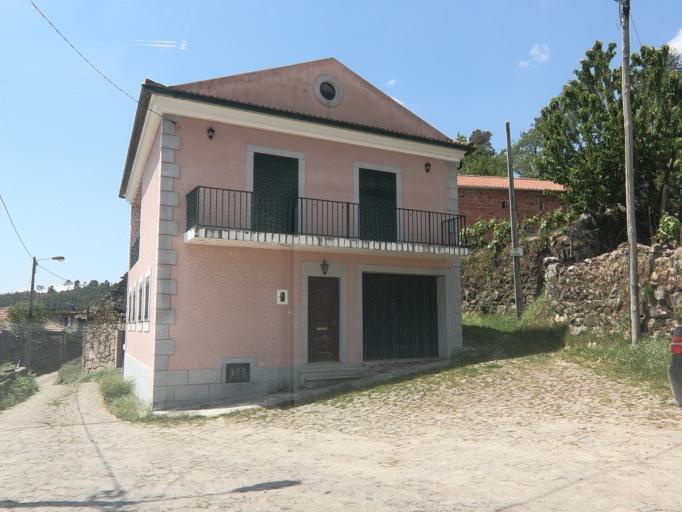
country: PT
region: Vila Real
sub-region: Vila Real
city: Vila Real
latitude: 41.3611
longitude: -7.7297
